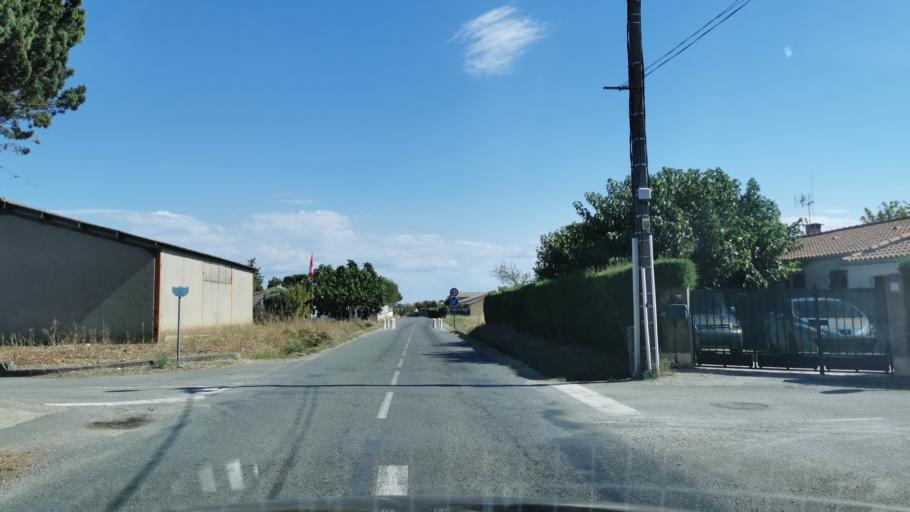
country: FR
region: Languedoc-Roussillon
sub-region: Departement de l'Aude
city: Peyriac-Minervois
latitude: 43.3120
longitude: 2.5585
